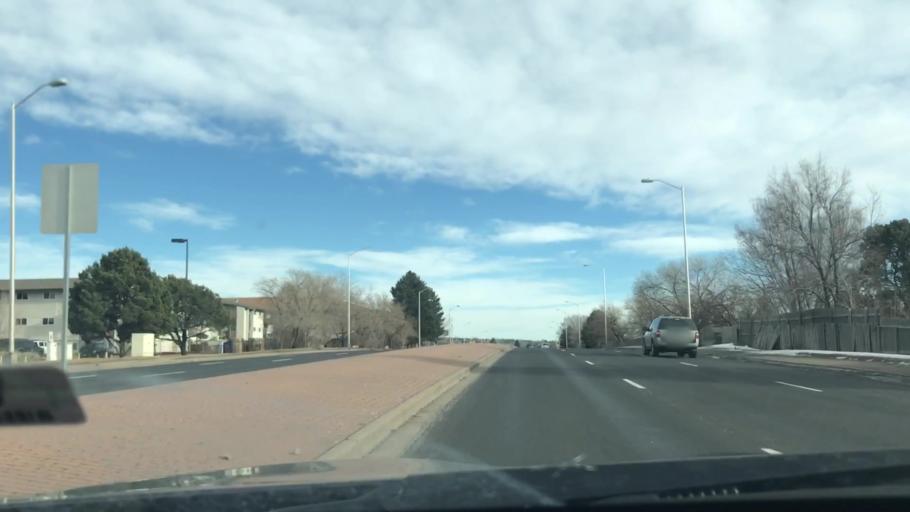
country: US
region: Colorado
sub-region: El Paso County
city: Colorado Springs
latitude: 38.9034
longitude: -104.7728
